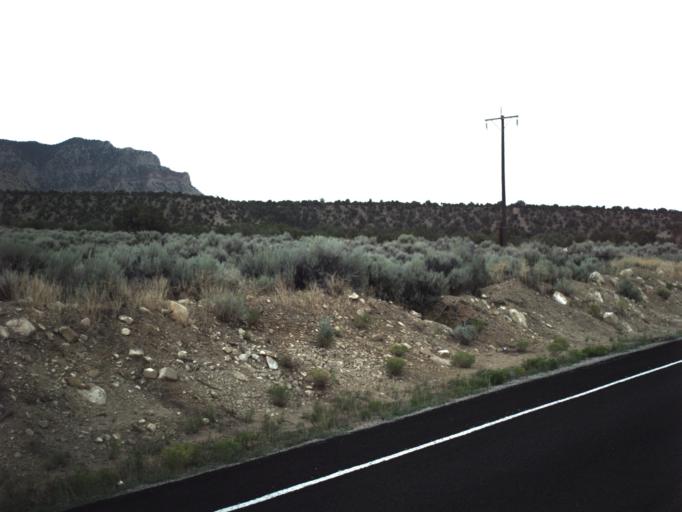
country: US
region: Utah
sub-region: Carbon County
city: East Carbon City
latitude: 39.5015
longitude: -110.3989
